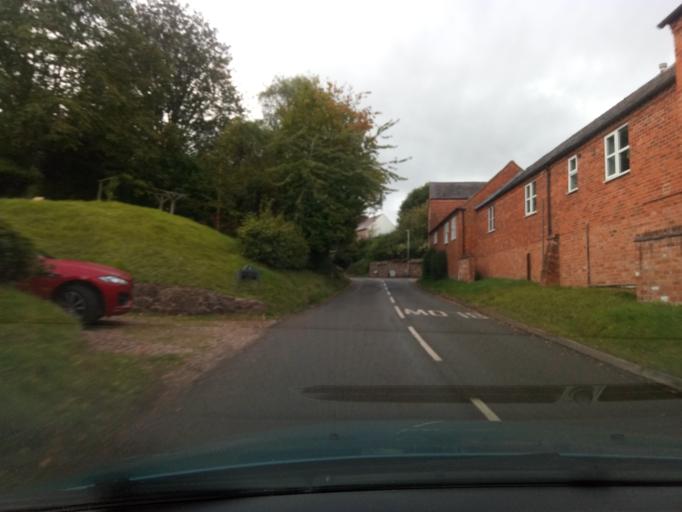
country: GB
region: England
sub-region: Leicestershire
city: Sileby
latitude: 52.7516
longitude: -1.0830
